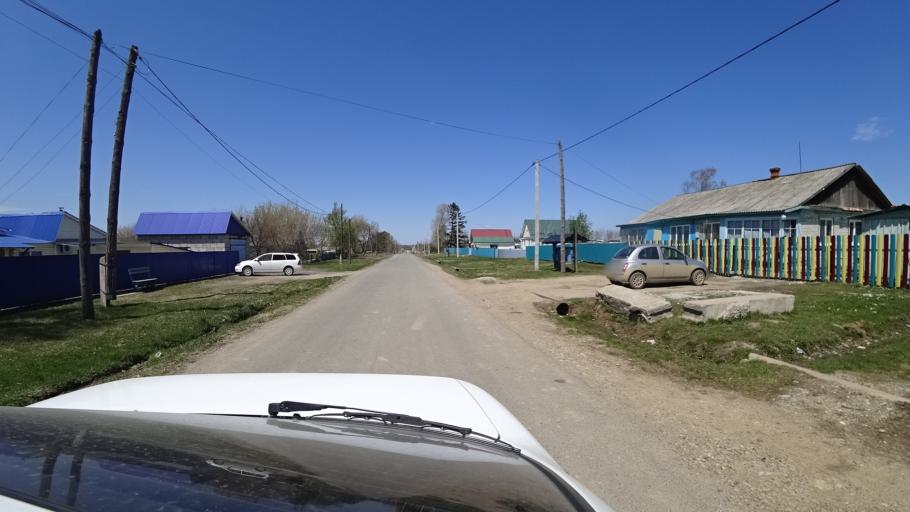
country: RU
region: Primorskiy
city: Dal'nerechensk
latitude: 45.7943
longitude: 133.7716
